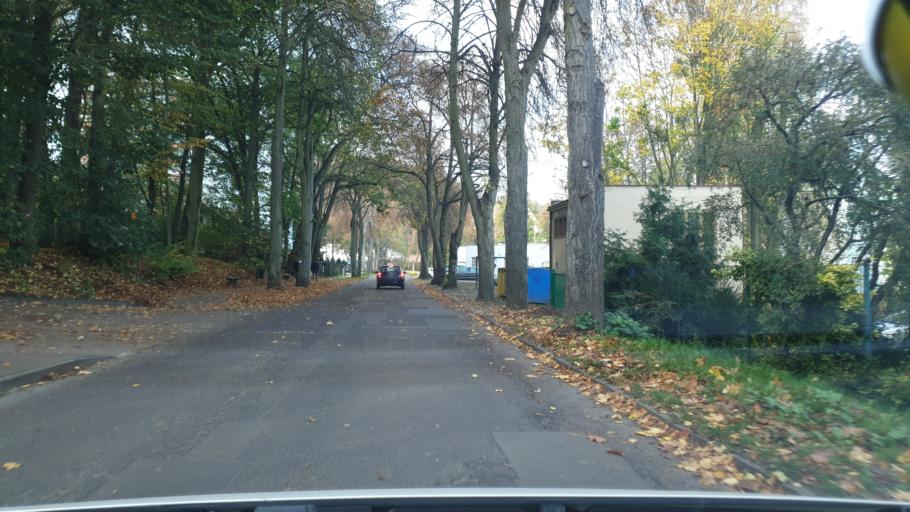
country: PL
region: Pomeranian Voivodeship
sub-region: Sopot
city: Sopot
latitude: 54.3886
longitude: 18.5702
